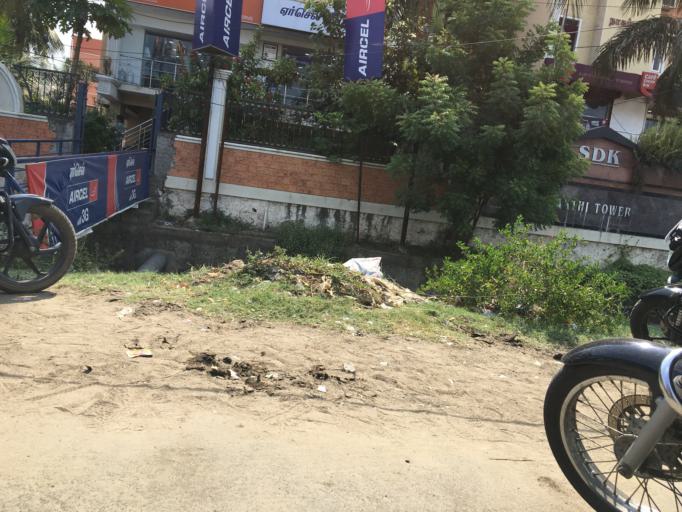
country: IN
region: Tamil Nadu
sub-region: Kancheepuram
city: Alandur
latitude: 12.9827
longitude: 80.2178
